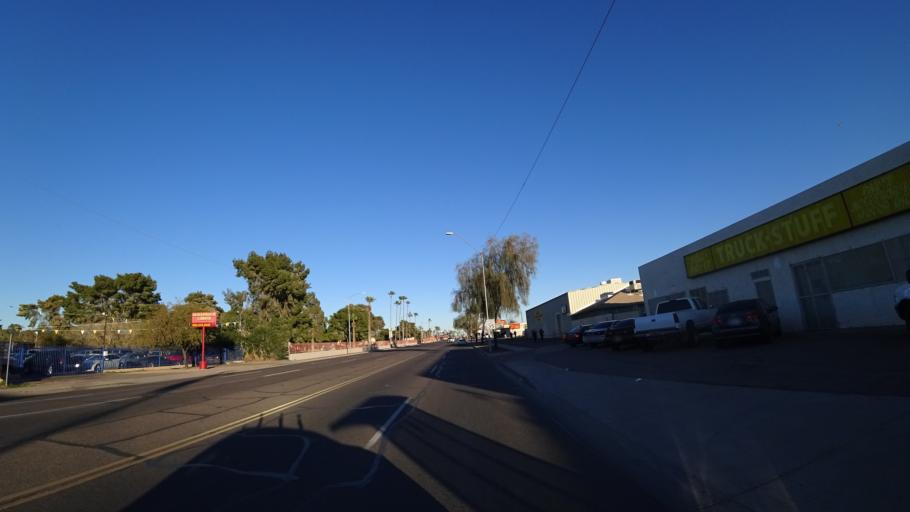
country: US
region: Arizona
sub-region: Maricopa County
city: Phoenix
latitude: 33.4511
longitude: -112.1129
